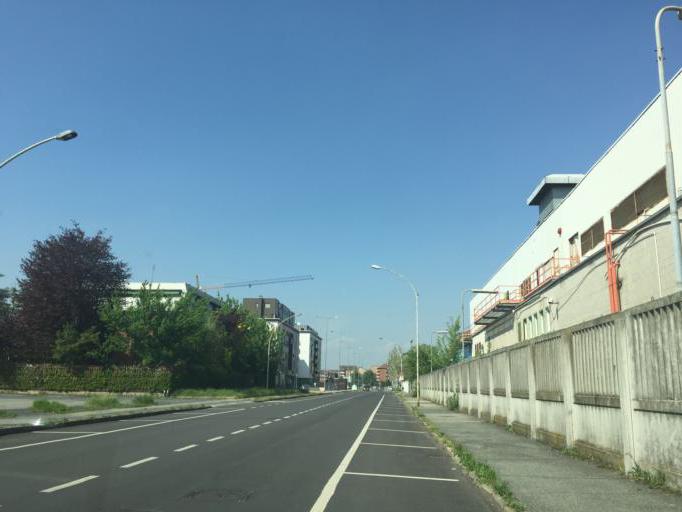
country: IT
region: Piedmont
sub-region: Provincia di Torino
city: Lesna
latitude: 45.0550
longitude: 7.6186
